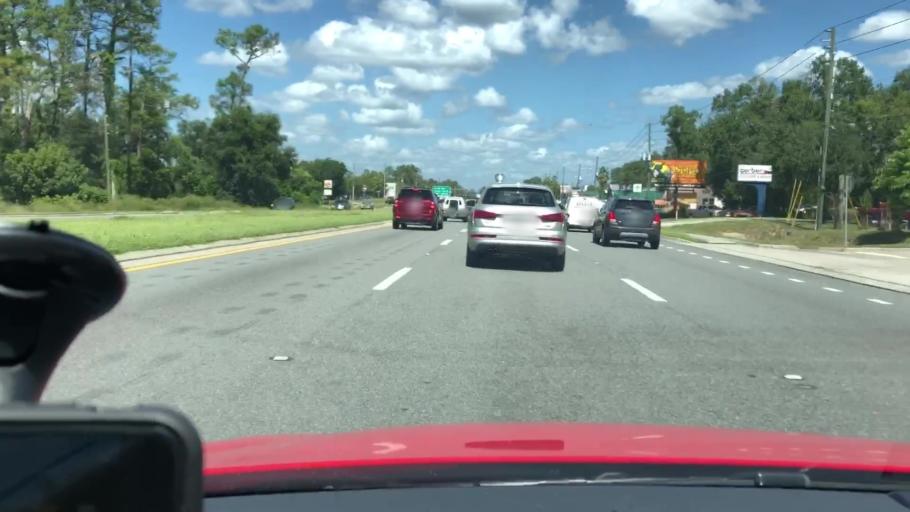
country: US
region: Florida
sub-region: Volusia County
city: De Land Southwest
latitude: 28.9939
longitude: -81.3023
